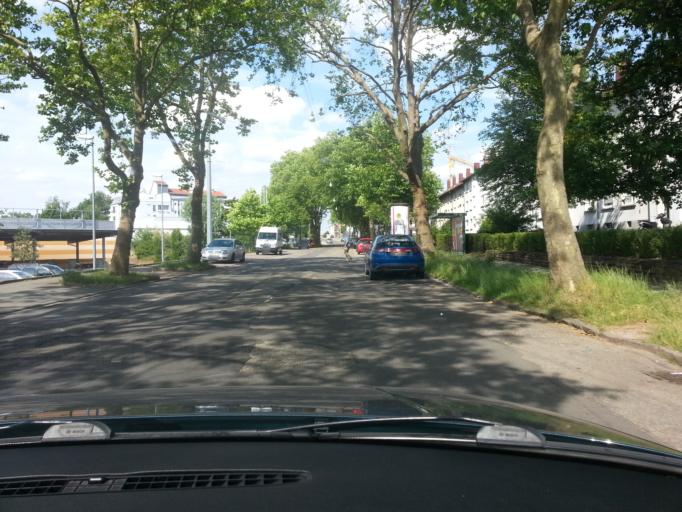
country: DE
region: Rheinland-Pfalz
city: Pirmasens
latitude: 49.1924
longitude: 7.5915
